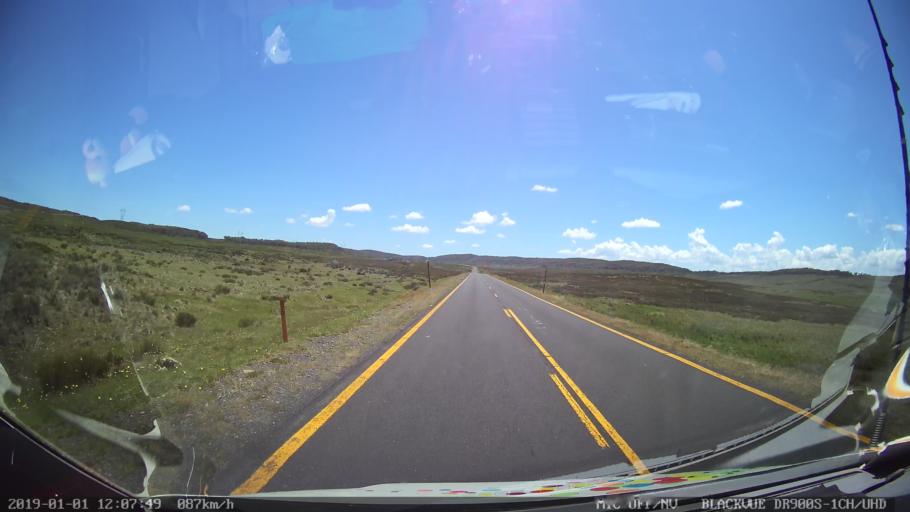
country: AU
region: New South Wales
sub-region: Tumut Shire
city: Tumut
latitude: -35.8282
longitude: 148.4916
